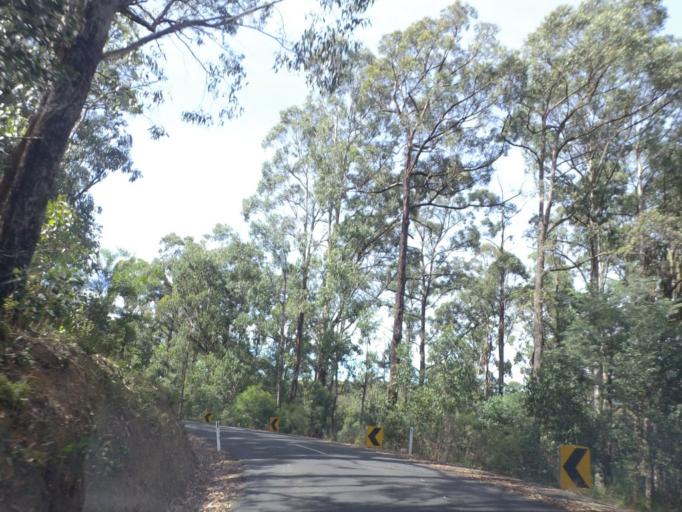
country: AU
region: Victoria
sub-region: Nillumbik
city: Saint Andrews
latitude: -37.5083
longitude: 145.3738
